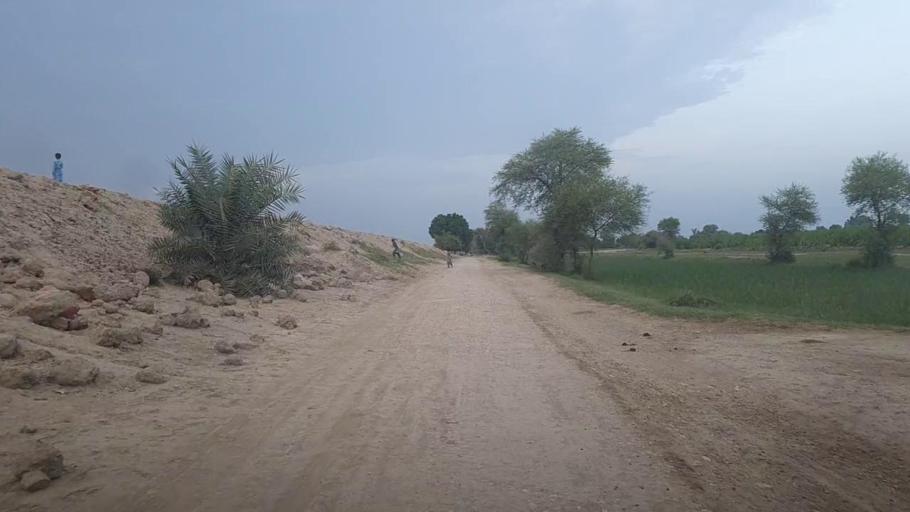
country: PK
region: Sindh
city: Kashmor
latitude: 28.3840
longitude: 69.7939
